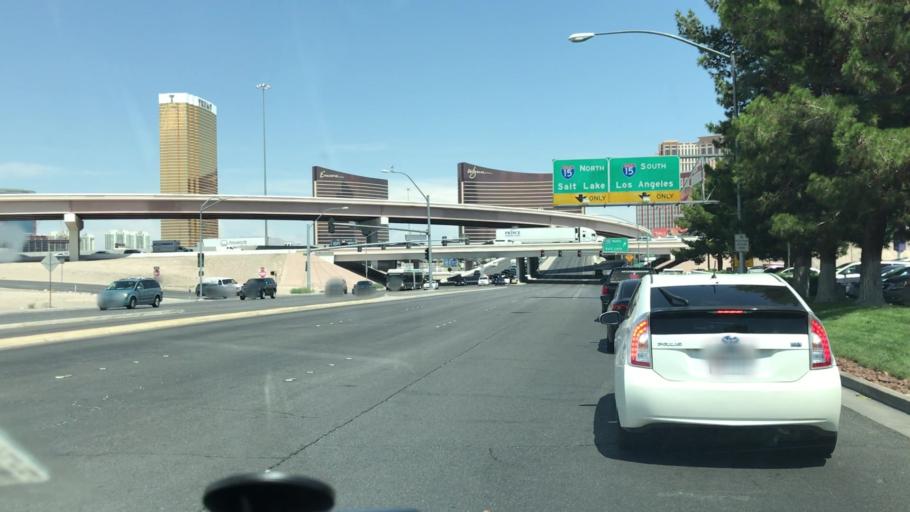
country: US
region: Nevada
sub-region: Clark County
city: Paradise
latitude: 36.1262
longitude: -115.1828
